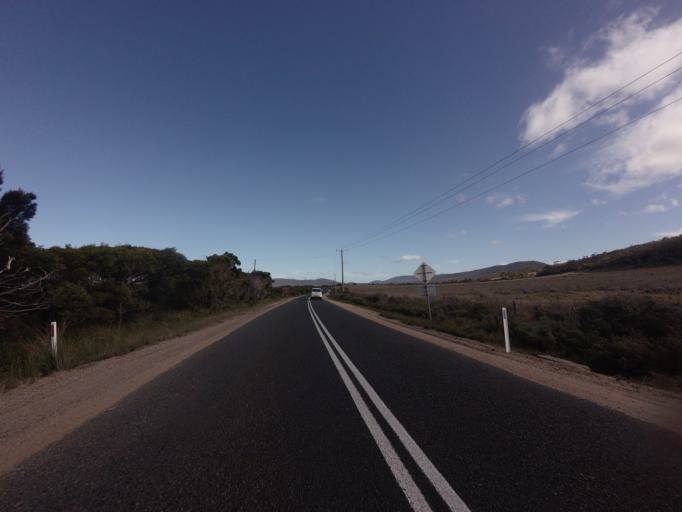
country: AU
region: Tasmania
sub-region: Break O'Day
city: St Helens
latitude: -41.8041
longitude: 148.2629
